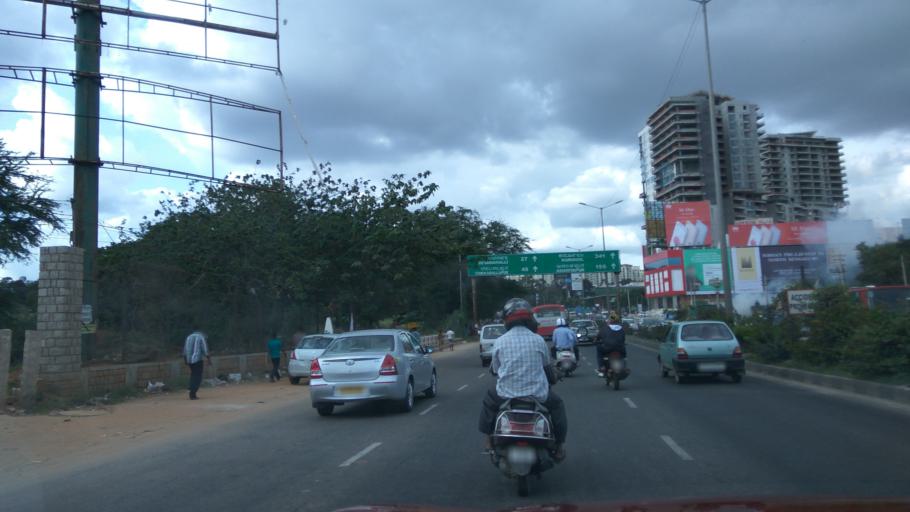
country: IN
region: Karnataka
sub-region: Bangalore Urban
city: Yelahanka
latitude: 13.0475
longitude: 77.5918
